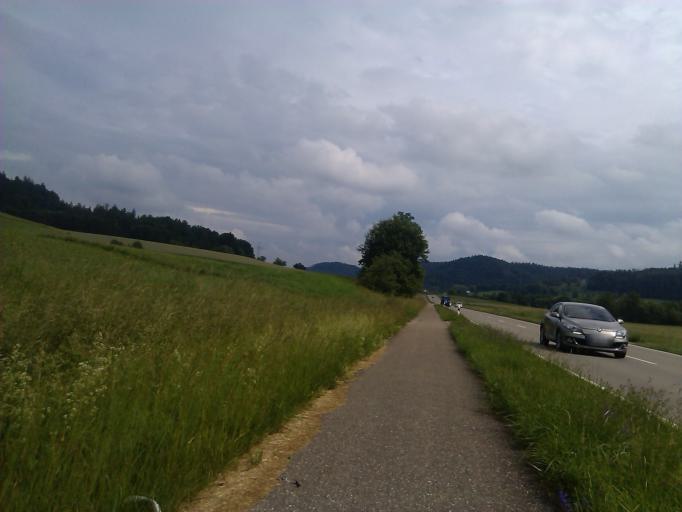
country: DE
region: Baden-Wuerttemberg
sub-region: Regierungsbezirk Stuttgart
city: Gaildorf
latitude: 48.9860
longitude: 9.7527
